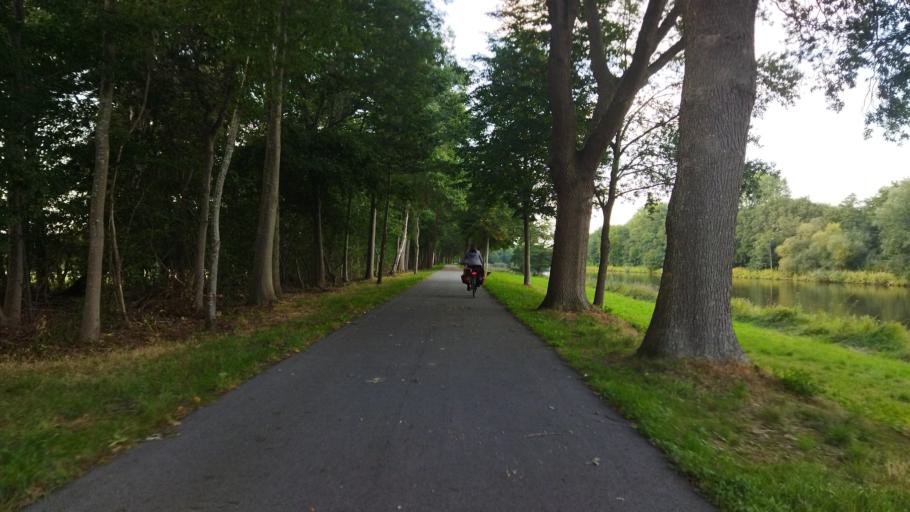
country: DE
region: Lower Saxony
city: Lehe
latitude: 52.9918
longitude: 7.3176
